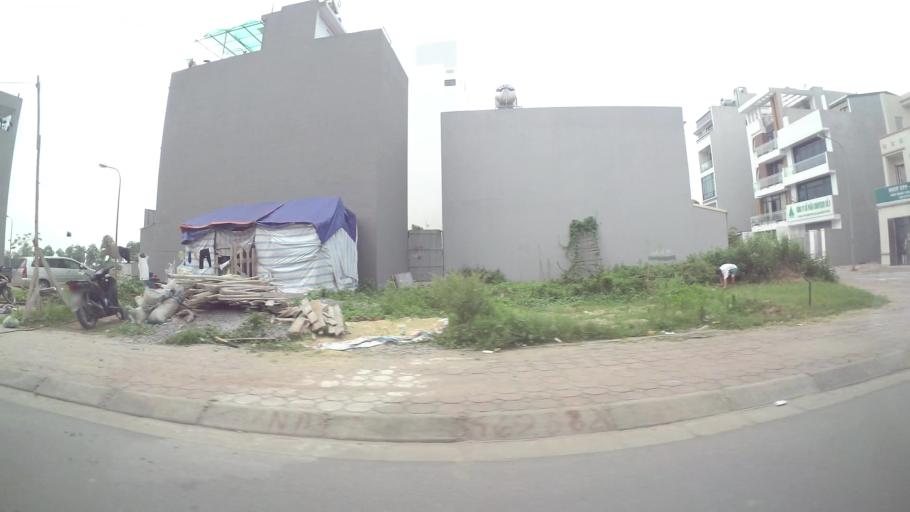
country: VN
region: Ha Noi
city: Trau Quy
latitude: 21.0383
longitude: 105.9310
